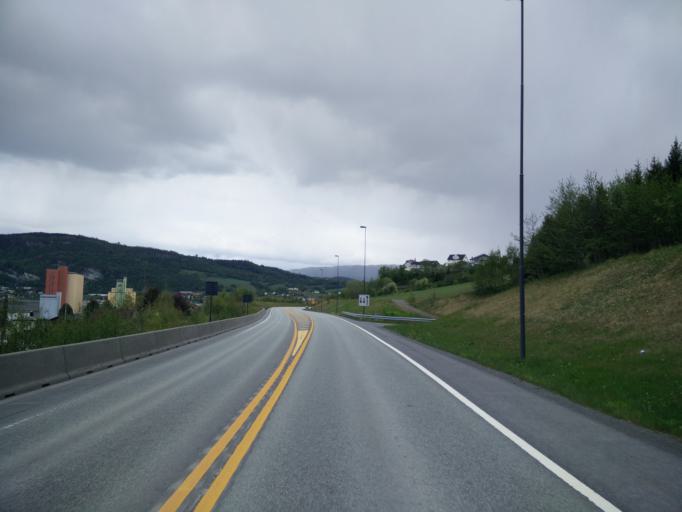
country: NO
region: Sor-Trondelag
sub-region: Skaun
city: Borsa
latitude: 63.3115
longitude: 10.1510
